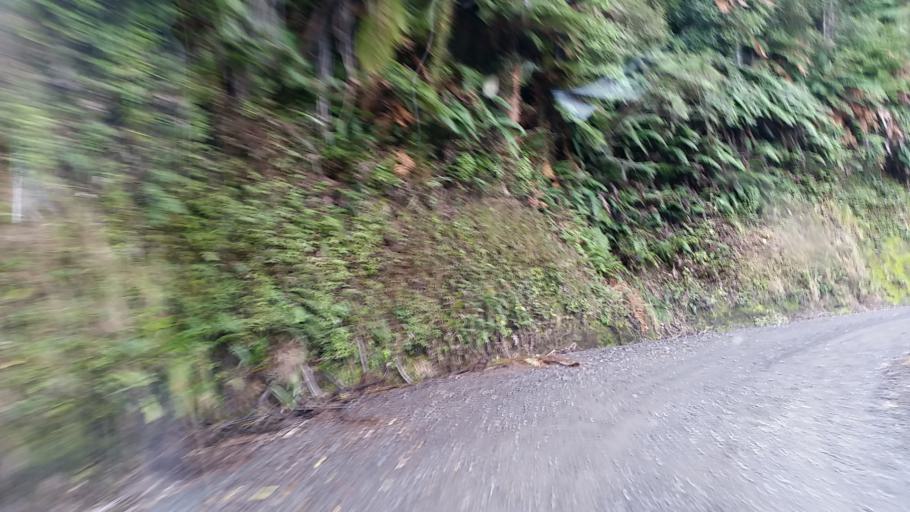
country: NZ
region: Taranaki
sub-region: New Plymouth District
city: Waitara
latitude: -39.1626
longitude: 174.5479
